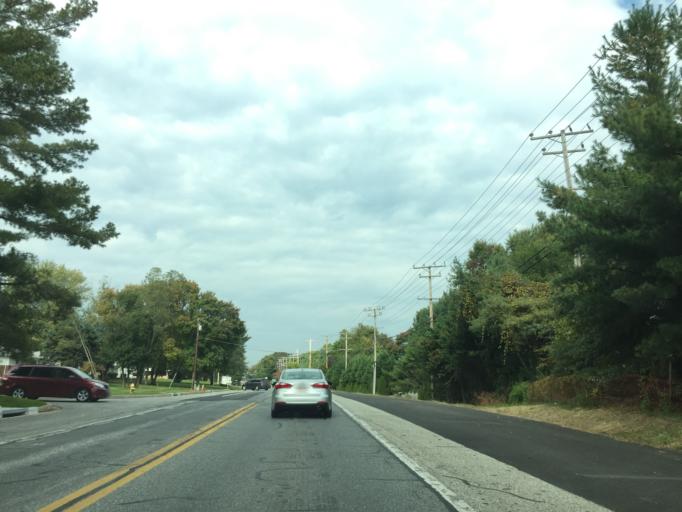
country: US
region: Maryland
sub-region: Harford County
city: Bel Air South
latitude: 39.4821
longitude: -76.3120
